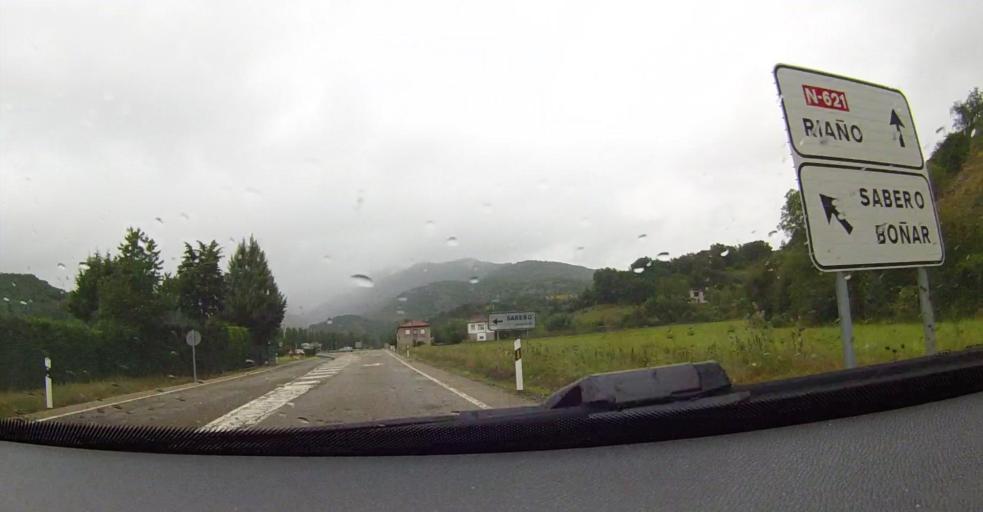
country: ES
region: Castille and Leon
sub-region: Provincia de Leon
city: Sabero
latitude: 42.8317
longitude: -5.1274
